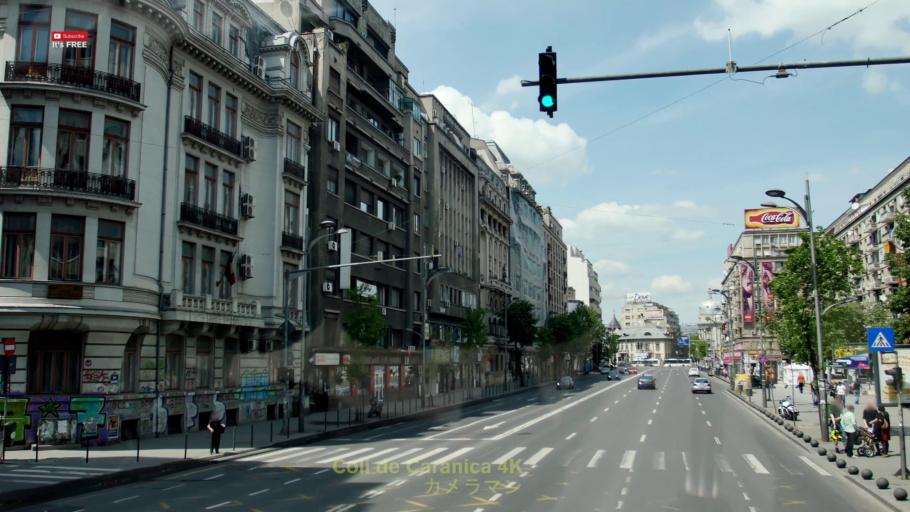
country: RO
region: Bucuresti
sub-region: Municipiul Bucuresti
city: Bucharest
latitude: 44.4447
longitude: 26.0979
